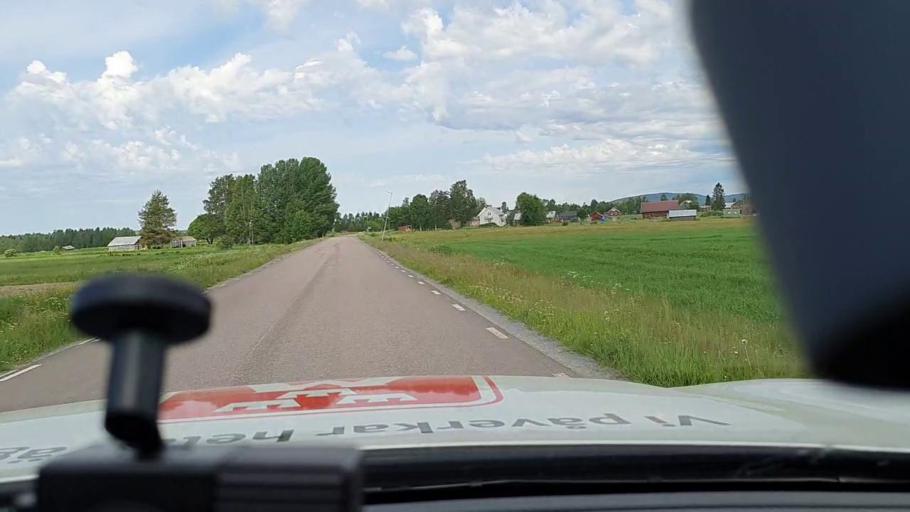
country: SE
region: Norrbotten
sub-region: Bodens Kommun
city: Saevast
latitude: 65.6844
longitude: 21.7930
